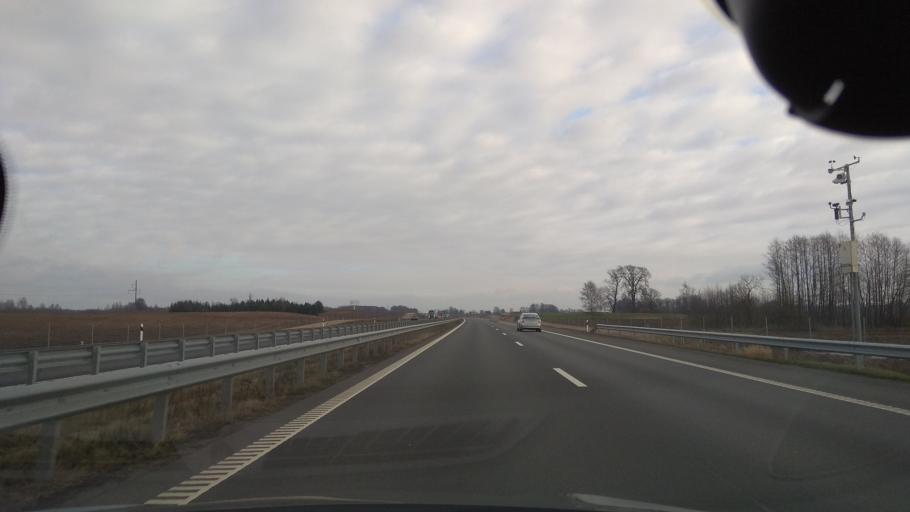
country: LT
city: Kazlu Ruda
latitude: 54.7162
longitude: 23.6536
